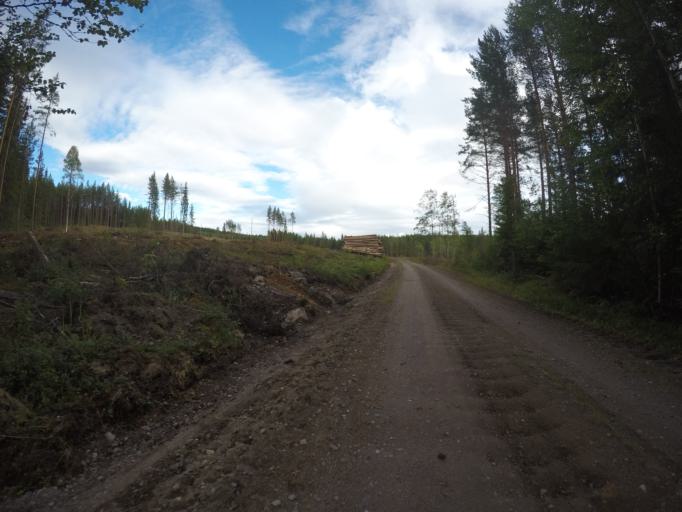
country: SE
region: Vaermland
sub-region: Filipstads Kommun
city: Lesjofors
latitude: 60.0122
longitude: 14.4003
